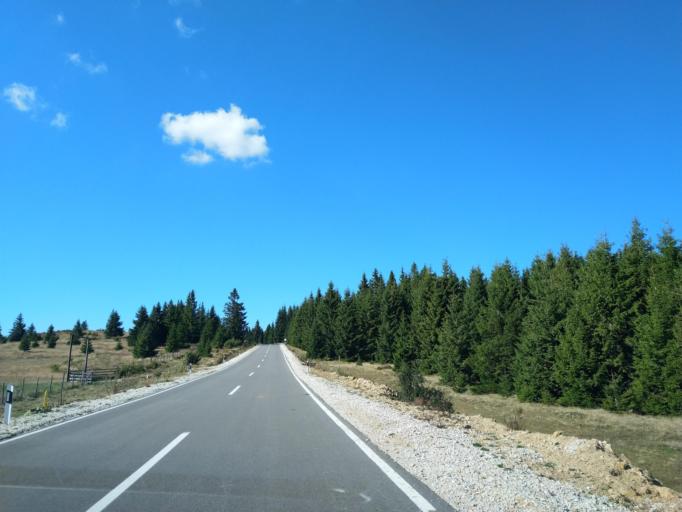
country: RS
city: Sokolovica
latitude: 43.3161
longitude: 20.2939
